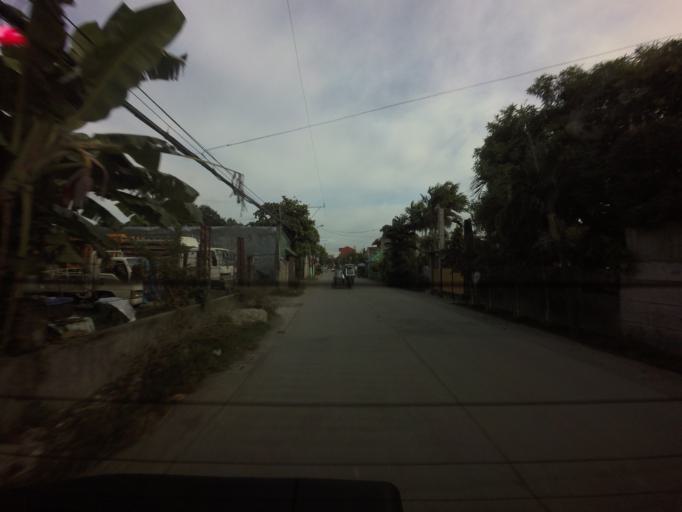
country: PH
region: Central Luzon
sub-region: Province of Bulacan
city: Obando
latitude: 14.7144
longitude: 120.9384
